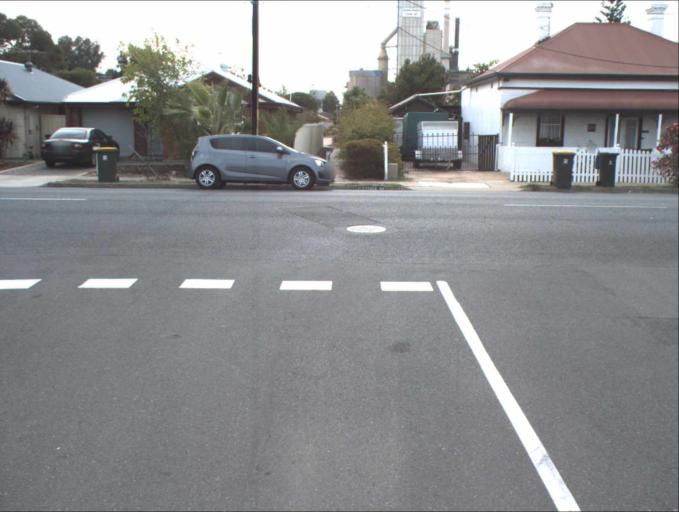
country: AU
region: South Australia
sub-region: Port Adelaide Enfield
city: Birkenhead
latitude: -34.8316
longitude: 138.4963
